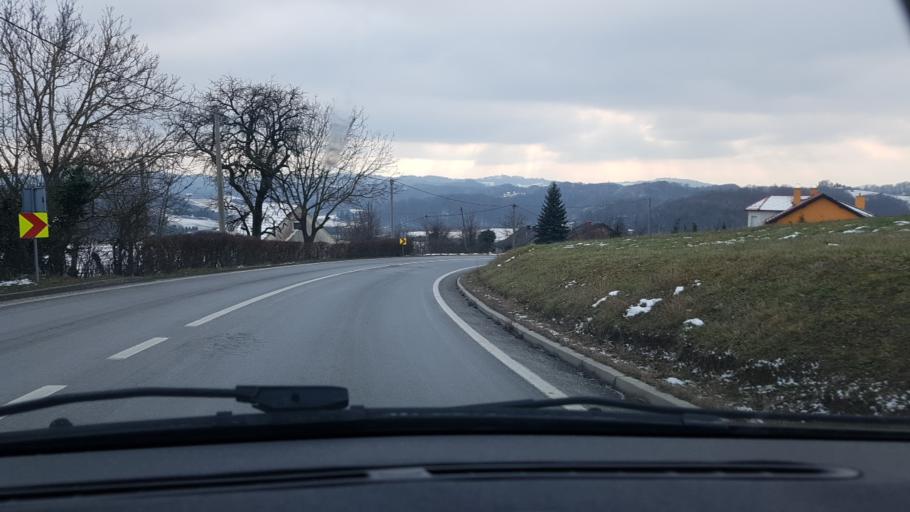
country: HR
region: Krapinsko-Zagorska
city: Mihovljan
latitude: 46.1547
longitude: 15.9639
